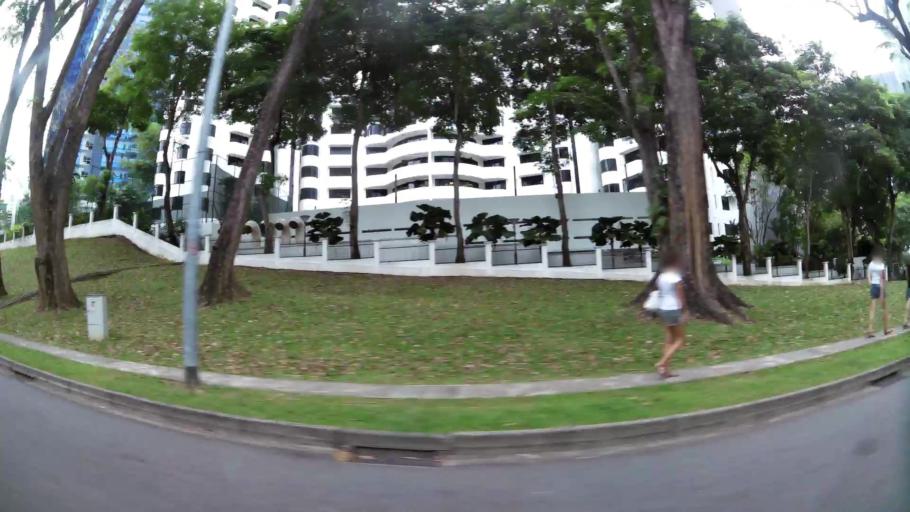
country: SG
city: Singapore
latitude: 1.3084
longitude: 103.8399
